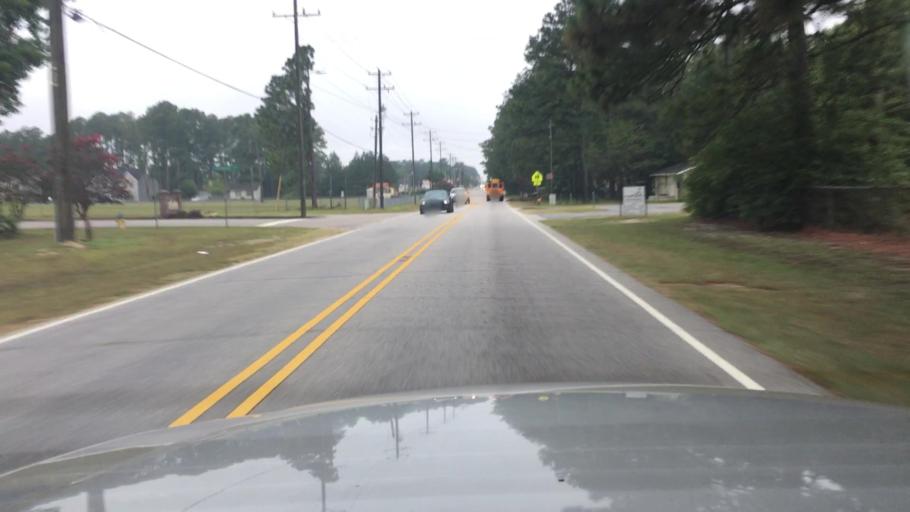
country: US
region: North Carolina
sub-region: Cumberland County
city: Hope Mills
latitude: 34.9767
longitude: -78.9811
